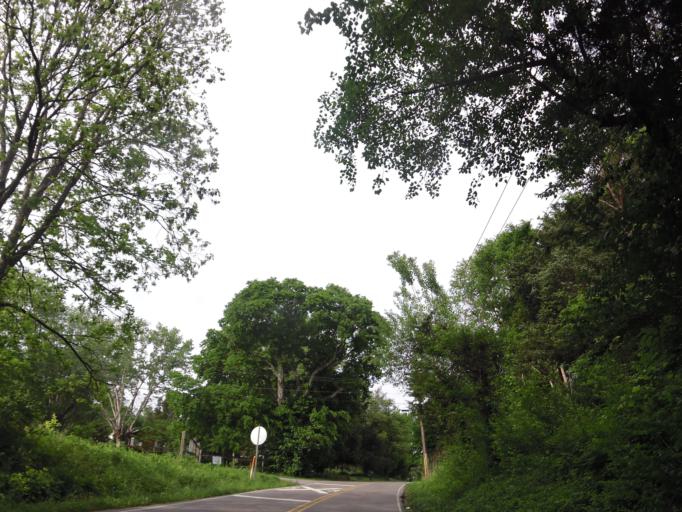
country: US
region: Tennessee
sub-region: Knox County
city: Knoxville
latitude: 36.0217
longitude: -83.8564
